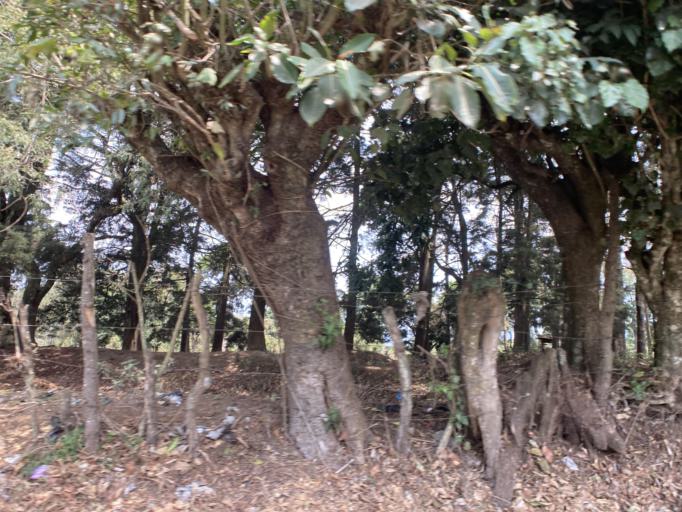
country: GT
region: Guatemala
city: Villa Canales
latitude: 14.4081
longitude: -90.5406
